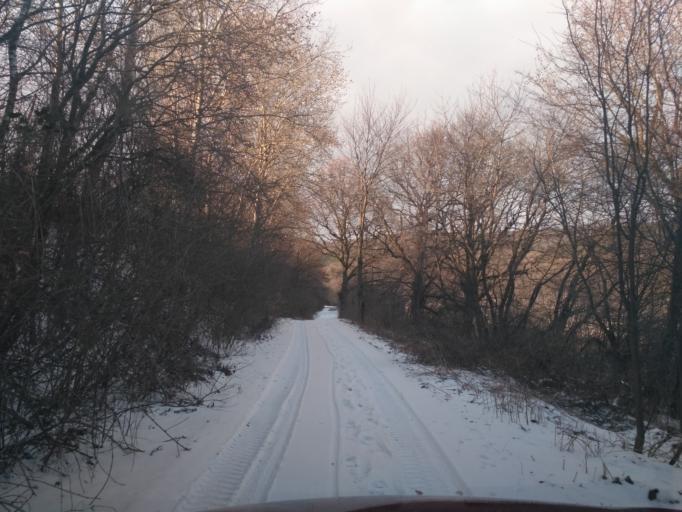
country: SK
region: Kosicky
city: Kosice
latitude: 48.7362
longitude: 21.1501
